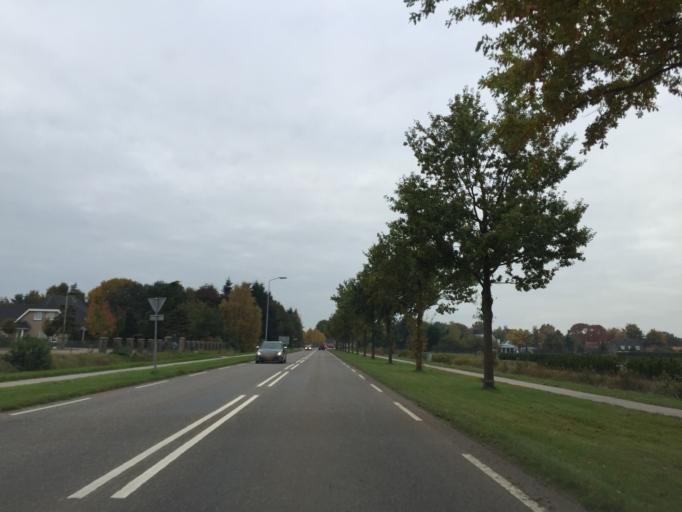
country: NL
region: North Brabant
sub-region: Gemeente Waalwijk
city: Waalwijk
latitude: 51.6646
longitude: 5.0535
